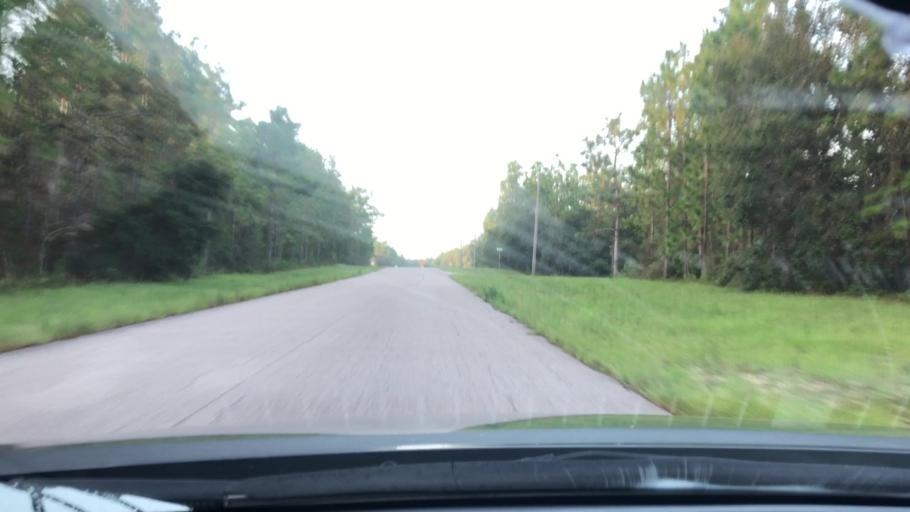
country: US
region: Florida
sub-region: Marion County
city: Belleview
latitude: 29.0286
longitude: -82.2403
